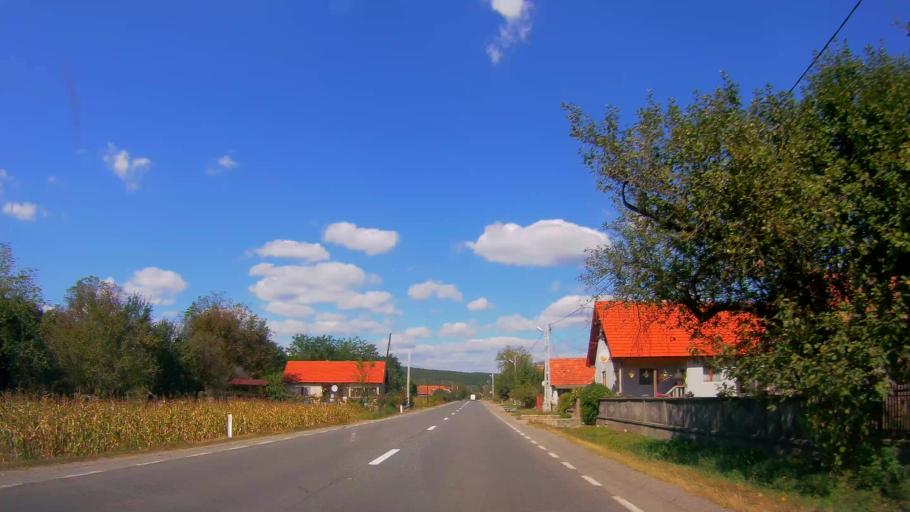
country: RO
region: Salaj
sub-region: Comuna Zimbor
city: Zimbor
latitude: 46.9809
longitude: 23.2523
